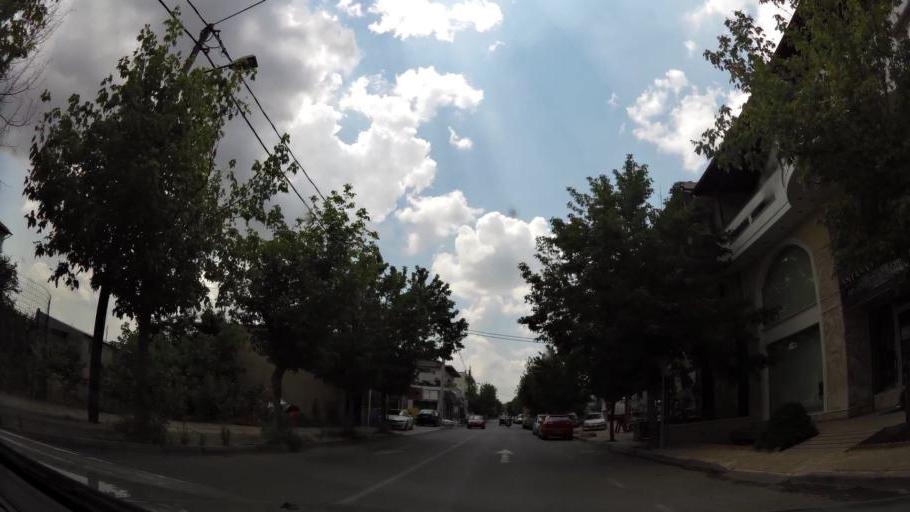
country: GR
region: West Macedonia
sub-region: Nomos Kozanis
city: Kozani
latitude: 40.3028
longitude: 21.8023
